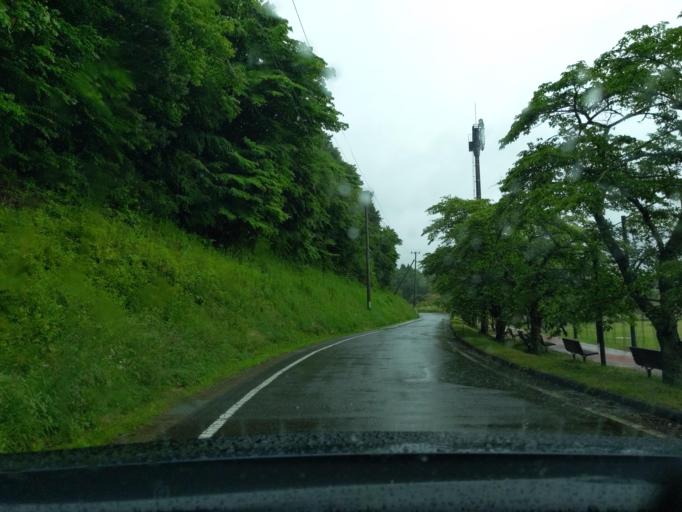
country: JP
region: Fukushima
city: Nihommatsu
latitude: 37.5933
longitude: 140.5729
